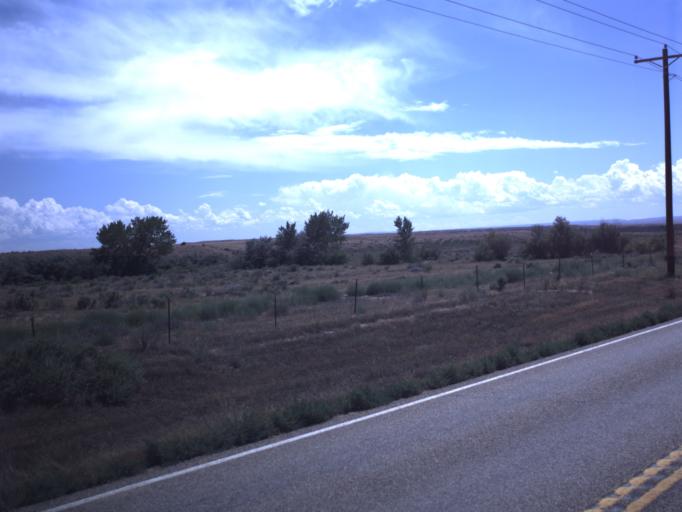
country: US
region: Utah
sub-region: Uintah County
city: Naples
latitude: 40.1418
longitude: -109.6640
